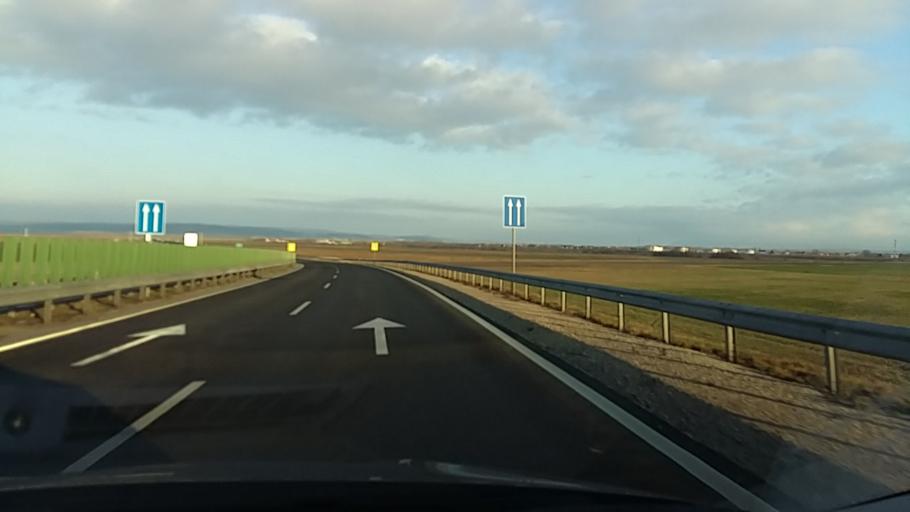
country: HU
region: Fejer
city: Szekesfehervar
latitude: 47.1843
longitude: 18.3766
